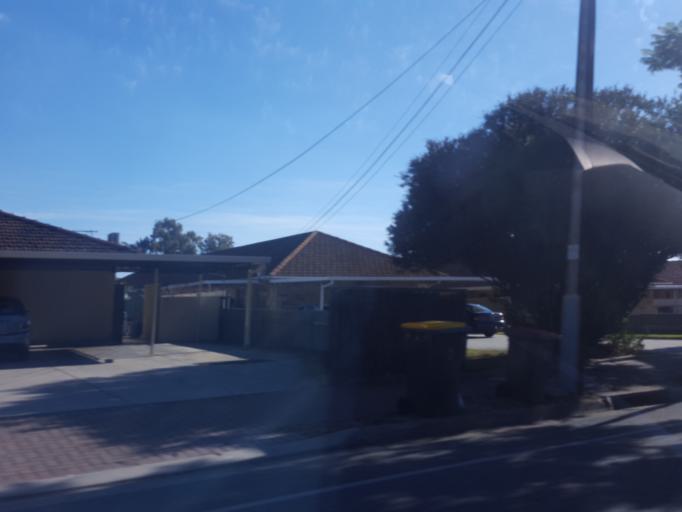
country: AU
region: South Australia
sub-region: Norwood Payneham St Peters
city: Payneham
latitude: -34.8932
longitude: 138.6413
